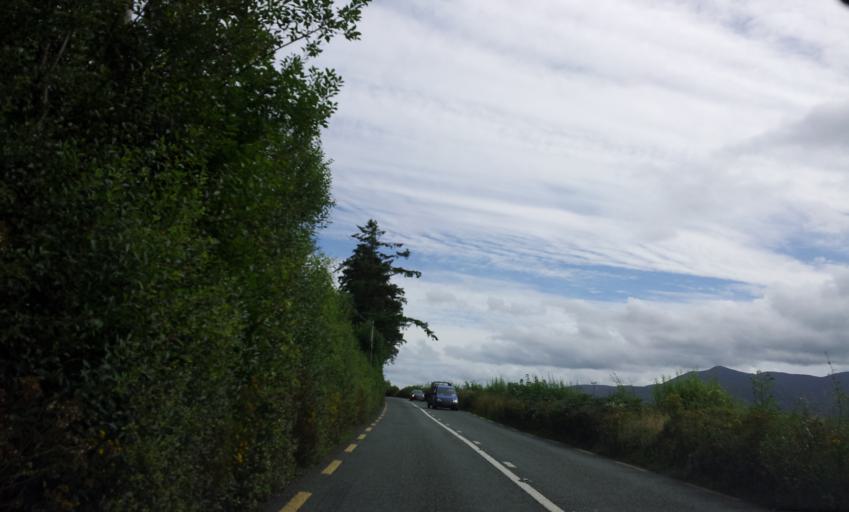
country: IE
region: Munster
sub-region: Ciarrai
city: Killorglin
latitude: 52.0860
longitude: -9.6807
